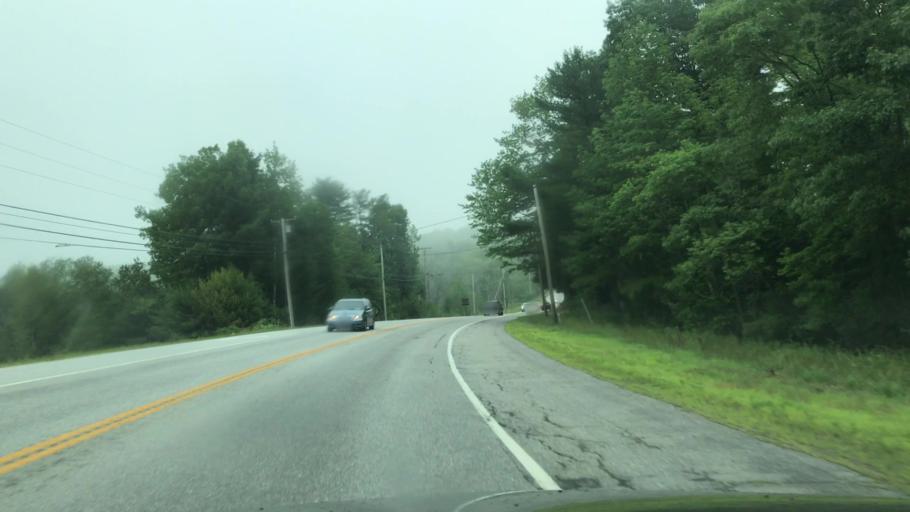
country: US
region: Maine
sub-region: Lincoln County
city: Nobleboro
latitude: 44.0927
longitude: -69.4683
